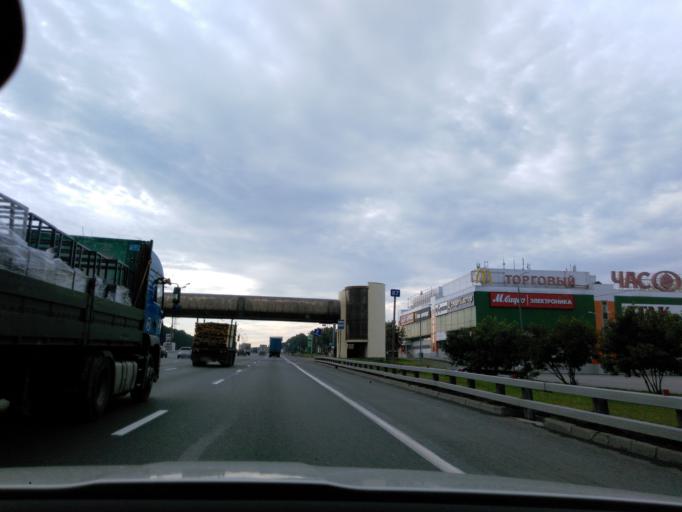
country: RU
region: Moscow
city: Bibirevo
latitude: 55.8998
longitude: 37.6271
